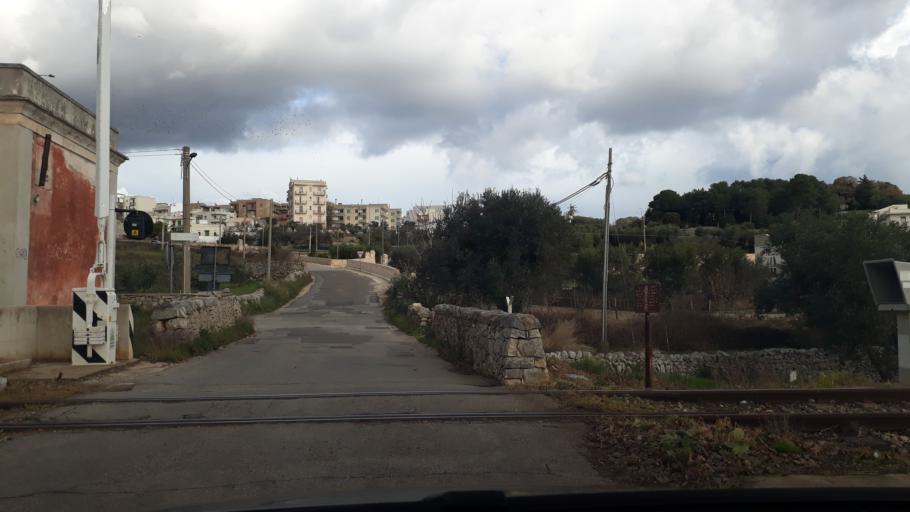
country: IT
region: Apulia
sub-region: Provincia di Brindisi
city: Cisternino
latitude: 40.7362
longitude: 17.4294
